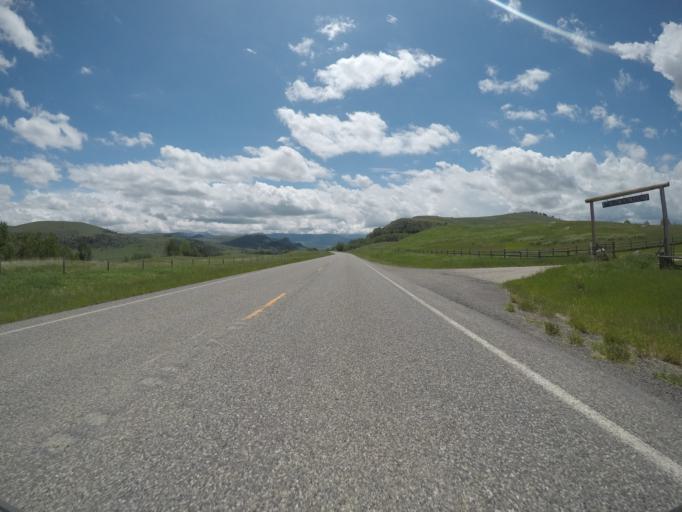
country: US
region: Montana
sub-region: Sweet Grass County
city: Big Timber
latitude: 45.6602
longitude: -110.1136
